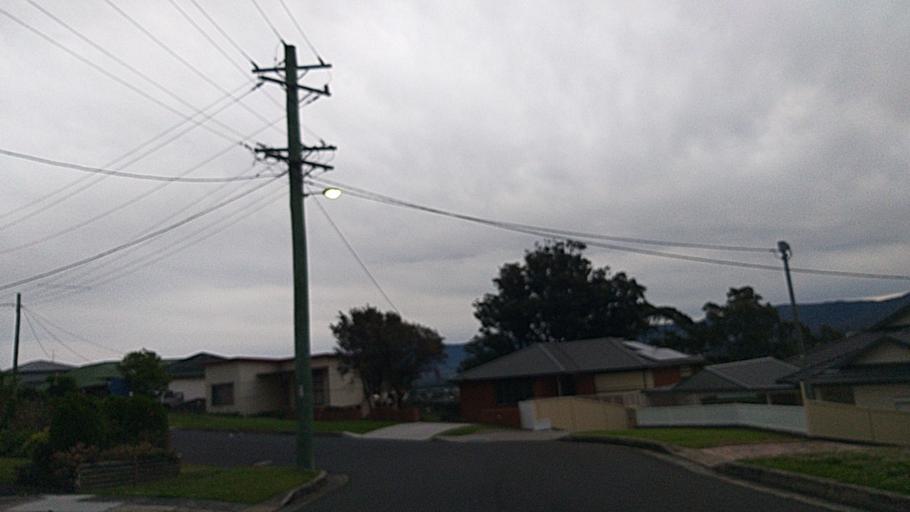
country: AU
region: New South Wales
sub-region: Wollongong
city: Lake Heights
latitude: -34.4816
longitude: 150.8634
